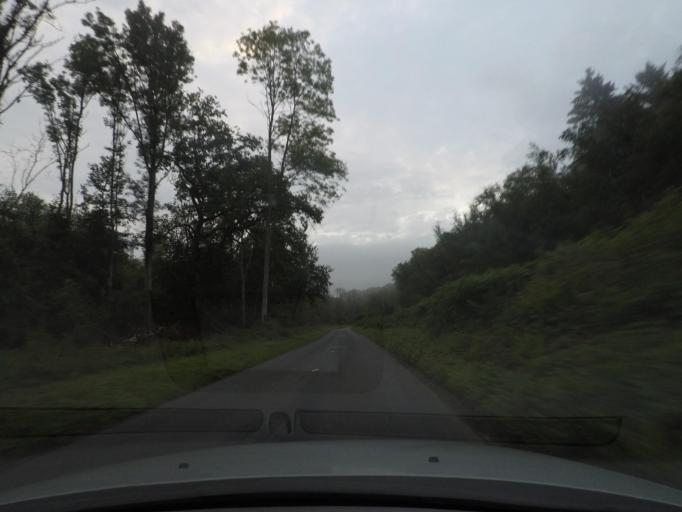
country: FR
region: Haute-Normandie
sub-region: Departement de la Seine-Maritime
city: Fontaine-le-Bourg
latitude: 49.5539
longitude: 1.1229
